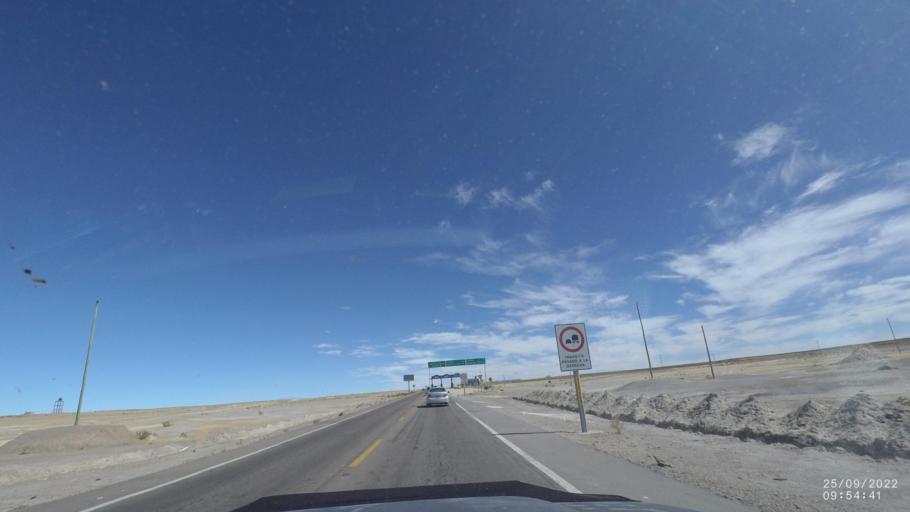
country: BO
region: Potosi
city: Colchani
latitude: -20.3321
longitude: -66.9162
